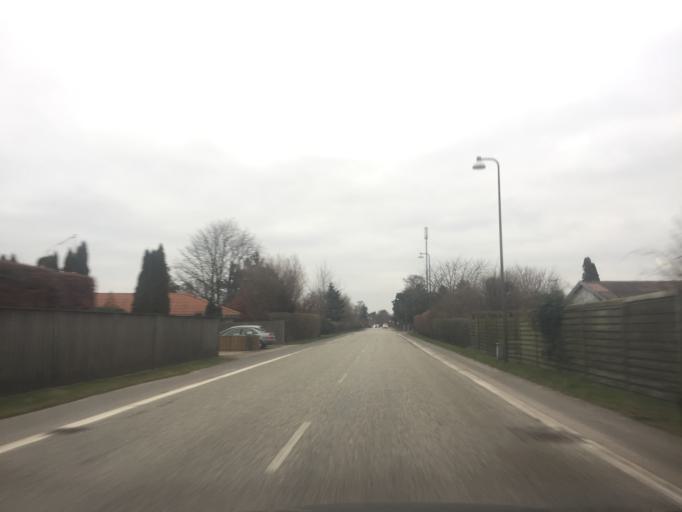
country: DK
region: Capital Region
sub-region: Halsnaes Kommune
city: Liseleje
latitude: 56.0051
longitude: 11.9834
